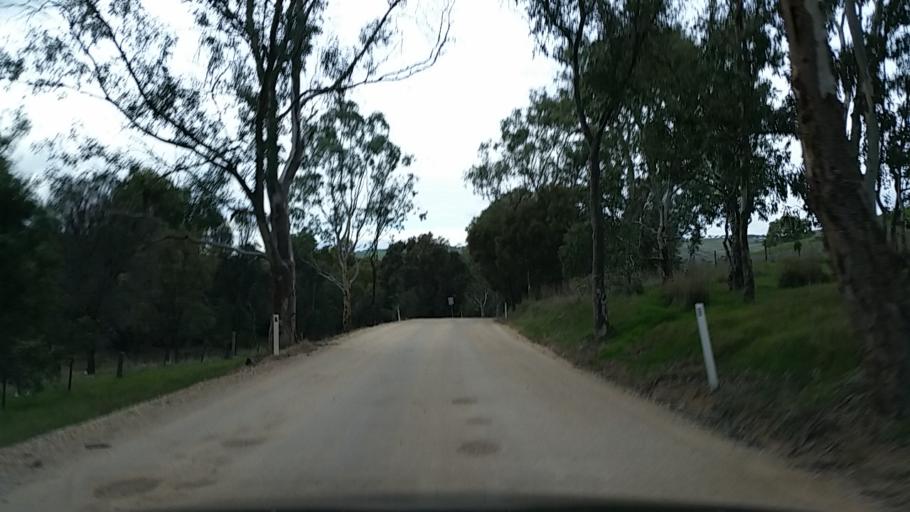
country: AU
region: South Australia
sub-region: Mount Barker
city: Nairne
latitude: -34.9545
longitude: 139.0124
